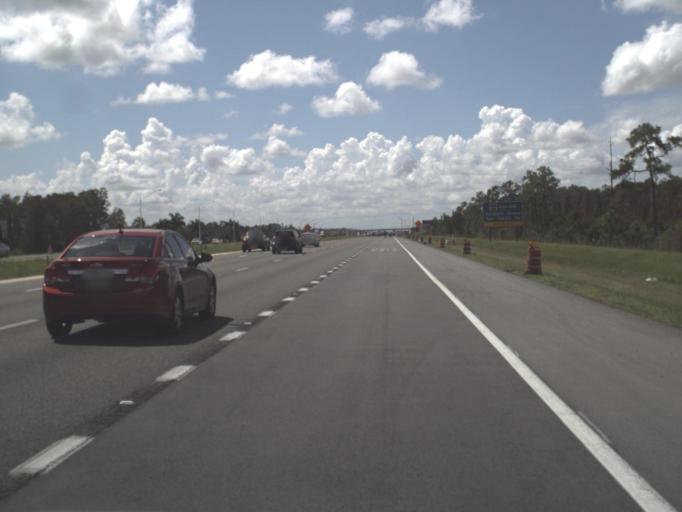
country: US
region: Florida
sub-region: Lee County
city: Three Oaks
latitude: 26.5309
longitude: -81.7951
